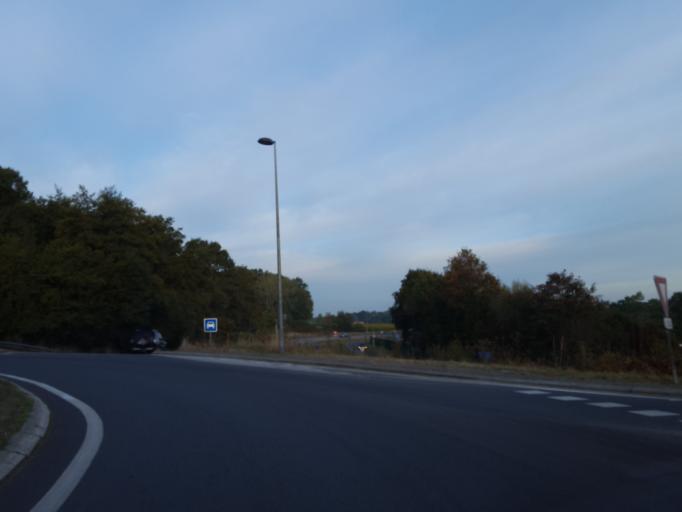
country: FR
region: Pays de la Loire
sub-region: Departement de la Loire-Atlantique
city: Haute-Goulaine
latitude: 47.2019
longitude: -1.4471
